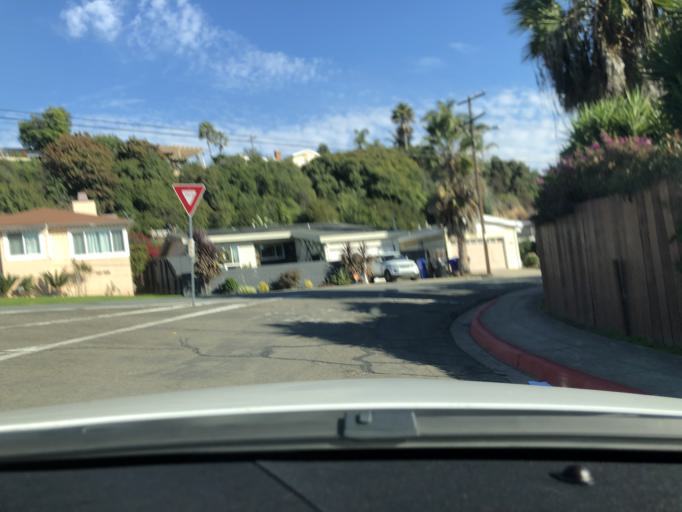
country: US
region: California
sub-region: San Diego County
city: Lemon Grove
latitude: 32.7527
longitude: -117.0719
